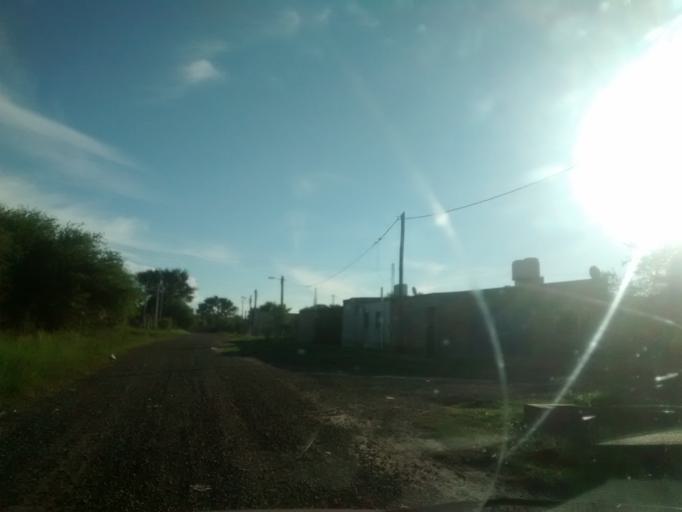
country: AR
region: Chaco
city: Fontana
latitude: -27.4609
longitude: -59.0318
